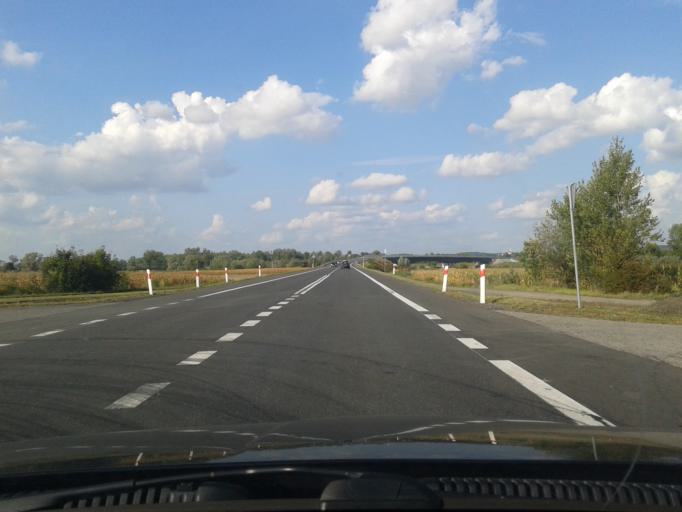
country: PL
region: Silesian Voivodeship
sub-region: Powiat wodzislawski
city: Olza
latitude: 49.9486
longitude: 18.3275
